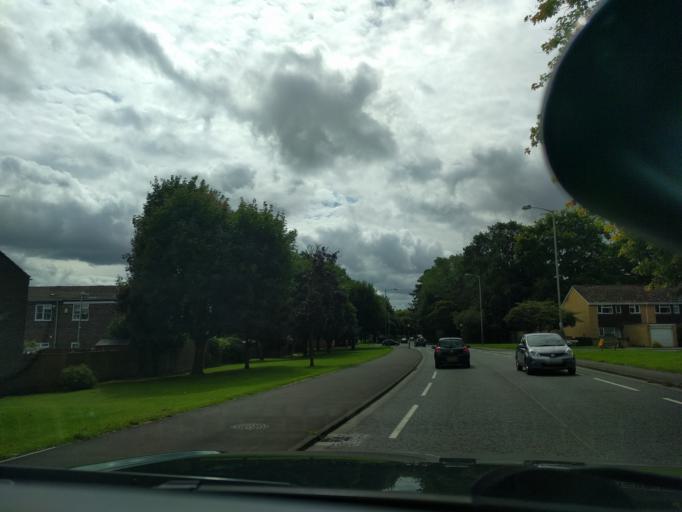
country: GB
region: England
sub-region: Wiltshire
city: Chippenham
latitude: 51.4552
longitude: -2.1381
